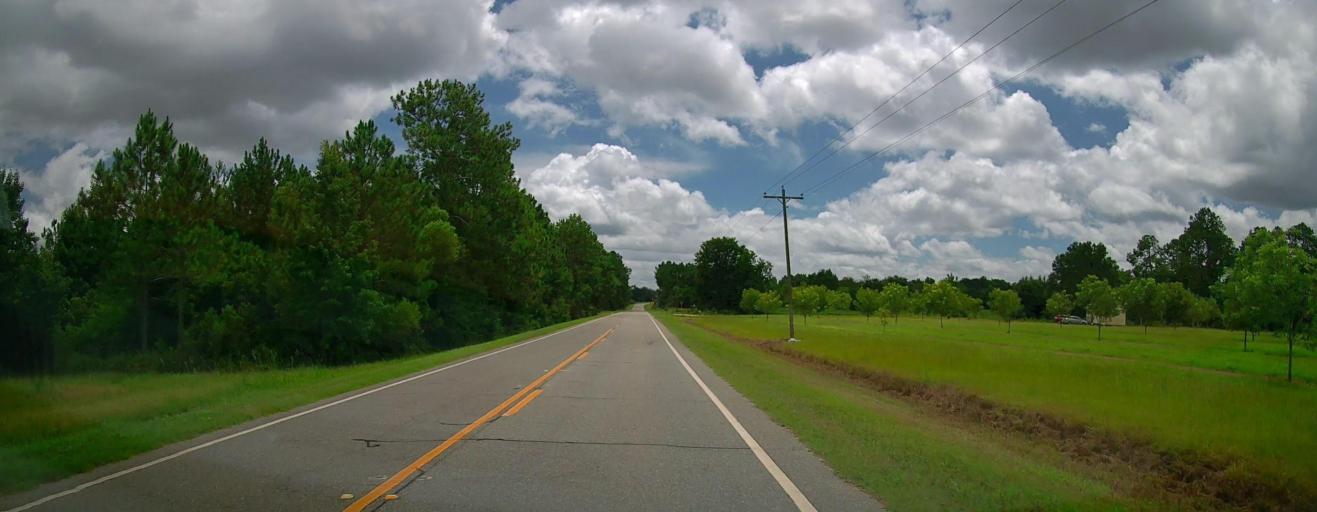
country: US
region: Georgia
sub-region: Wilcox County
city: Rochelle
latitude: 31.9652
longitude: -83.5450
